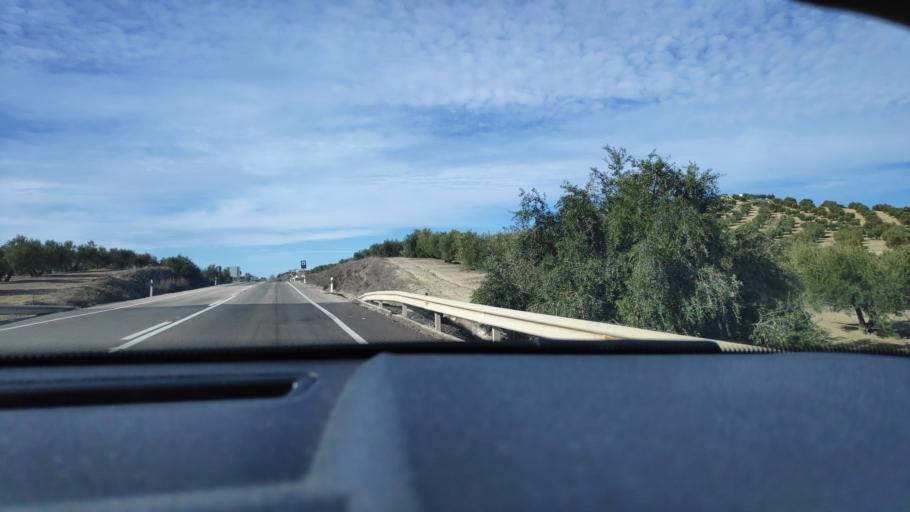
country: ES
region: Andalusia
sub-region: Provincia de Jaen
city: Porcuna
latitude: 37.8653
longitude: -4.1609
